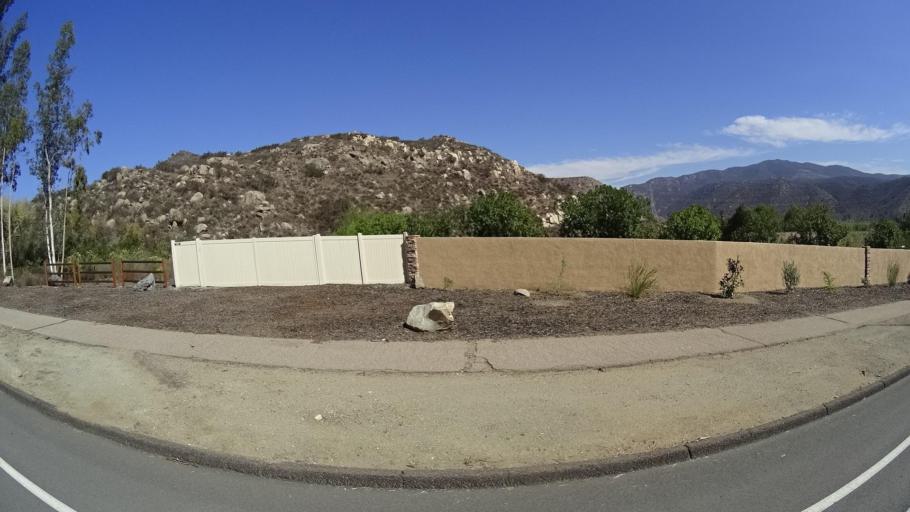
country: US
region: California
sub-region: San Diego County
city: Rancho San Diego
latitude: 32.7600
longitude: -116.9068
